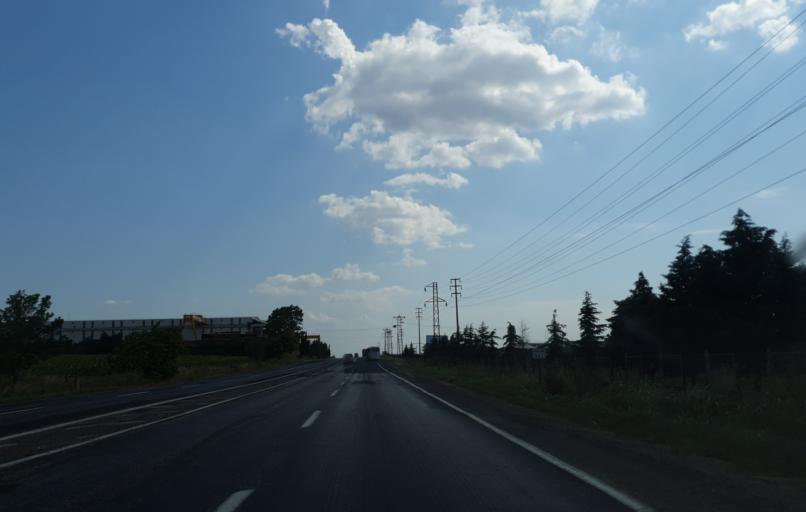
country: TR
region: Kirklareli
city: Buyukkaristiran
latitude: 41.2531
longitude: 27.5434
